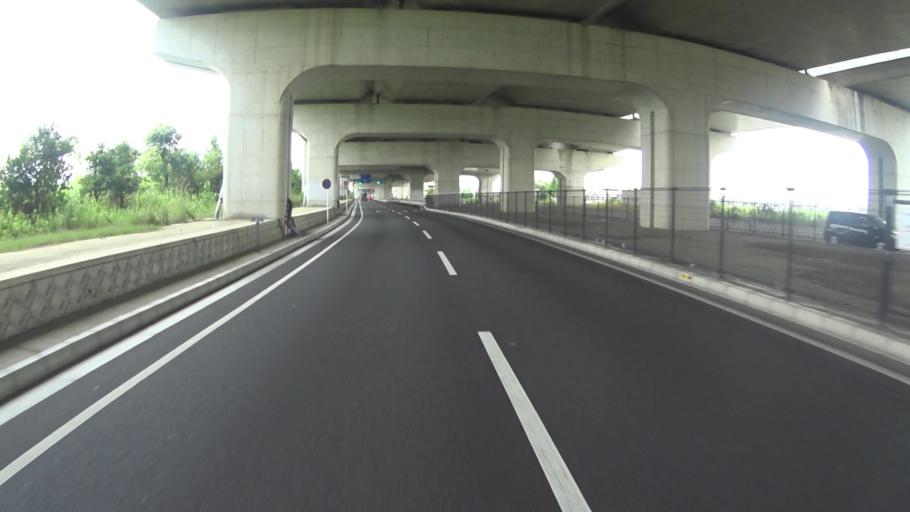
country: JP
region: Kyoto
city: Yawata
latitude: 34.8928
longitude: 135.7496
